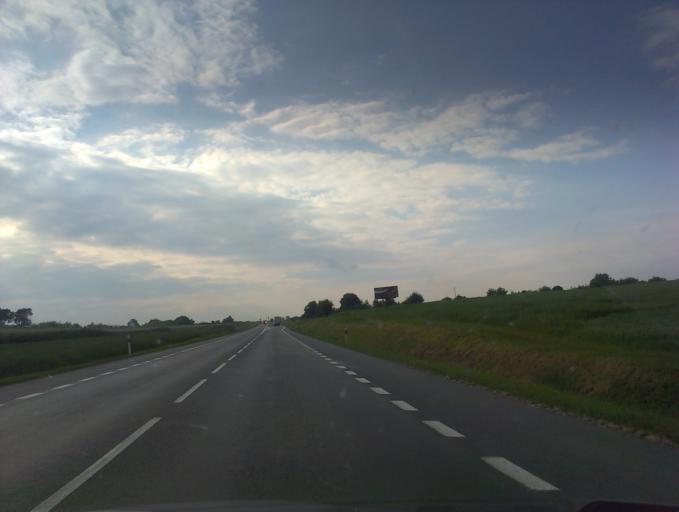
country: PL
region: Lower Silesian Voivodeship
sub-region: Powiat trzebnicki
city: Trzebnica
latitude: 51.2924
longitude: 17.0421
